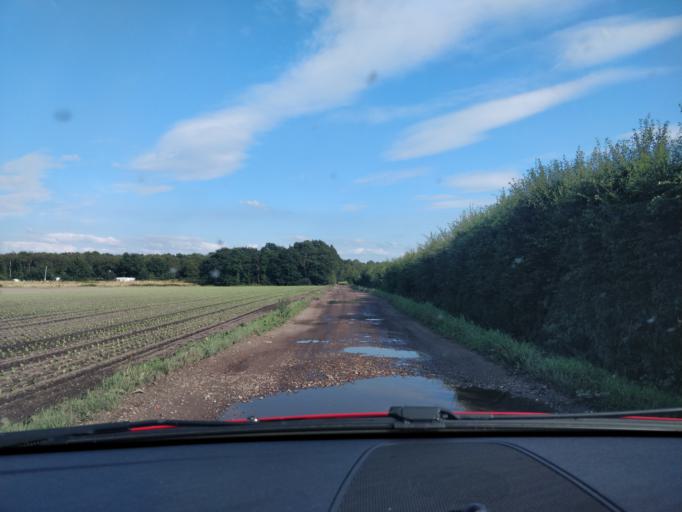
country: GB
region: England
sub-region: Lancashire
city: Banks
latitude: 53.6553
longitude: -2.9032
